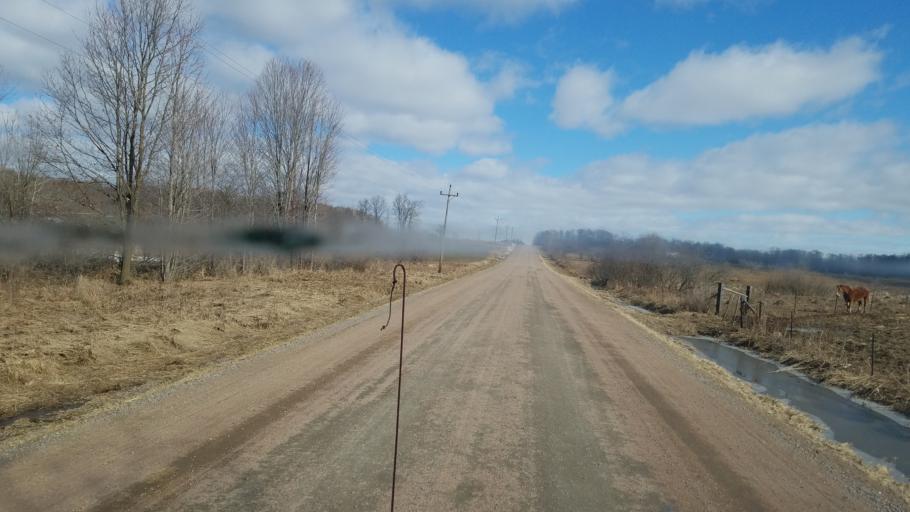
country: US
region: Wisconsin
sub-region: Clark County
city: Loyal
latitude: 44.6336
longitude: -90.4358
